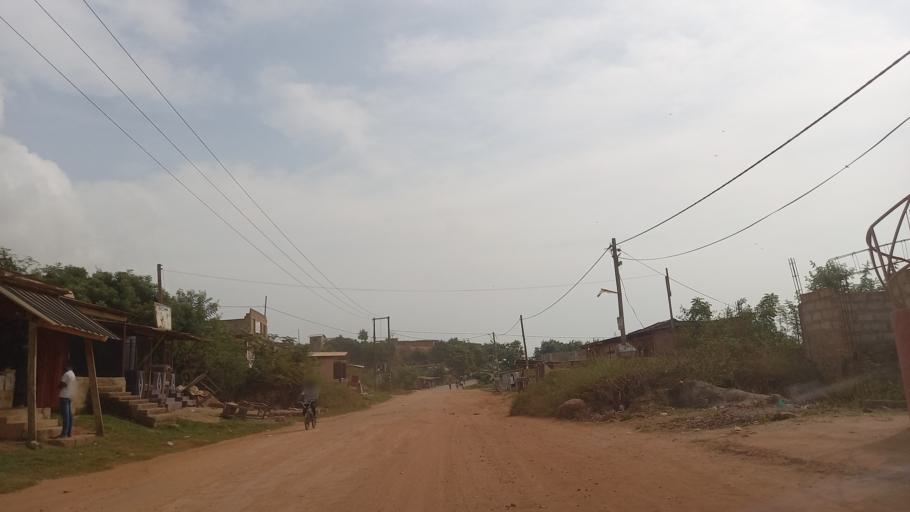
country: GH
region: Western
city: Shama Junction
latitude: 4.9766
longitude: -1.6470
